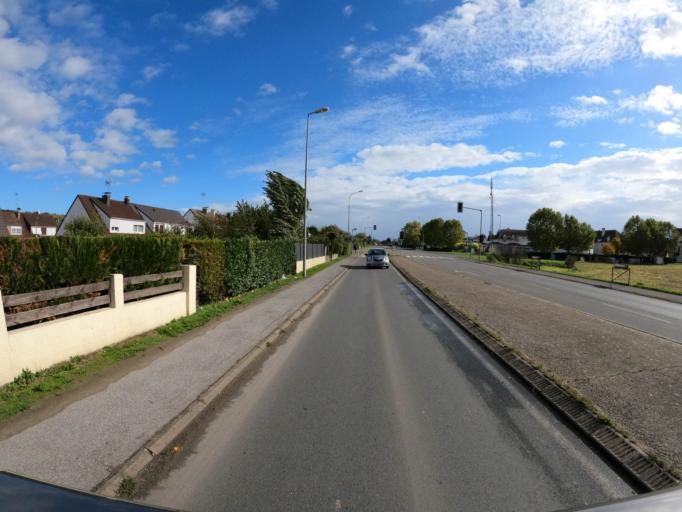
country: FR
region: Ile-de-France
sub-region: Departement de Seine-et-Marne
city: Montry
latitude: 48.8845
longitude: 2.8397
